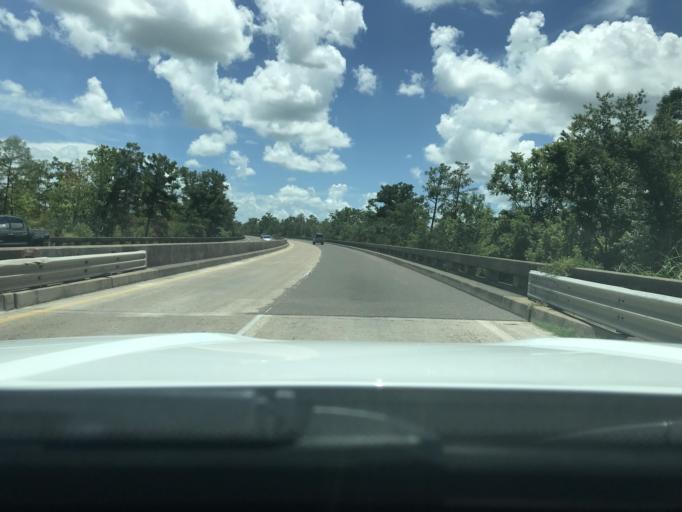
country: US
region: Louisiana
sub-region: Calcasieu Parish
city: Moss Bluff
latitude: 30.2968
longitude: -93.1952
